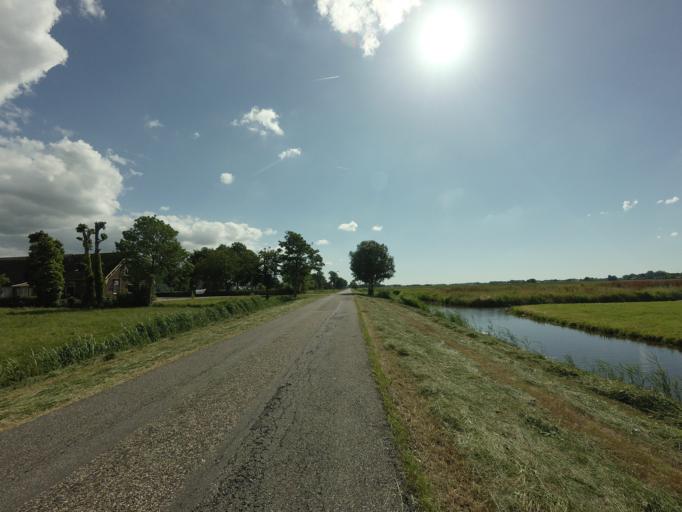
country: NL
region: Utrecht
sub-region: Gemeente De Ronde Venen
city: Mijdrecht
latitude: 52.2324
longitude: 4.8723
